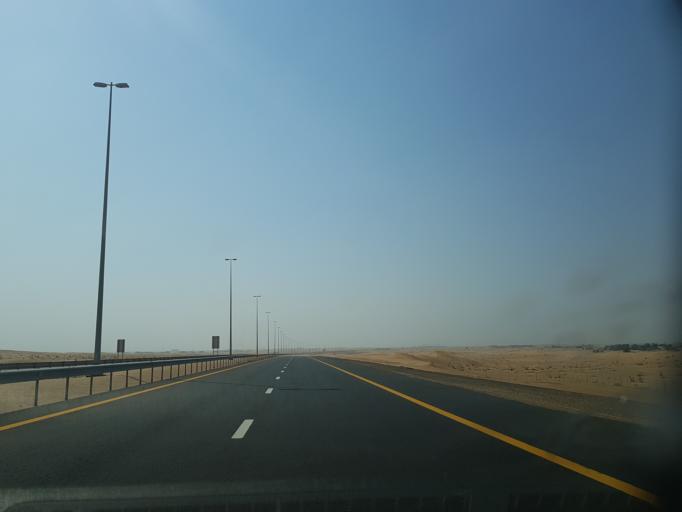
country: AE
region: Ash Shariqah
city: Sharjah
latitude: 25.2707
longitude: 55.6419
